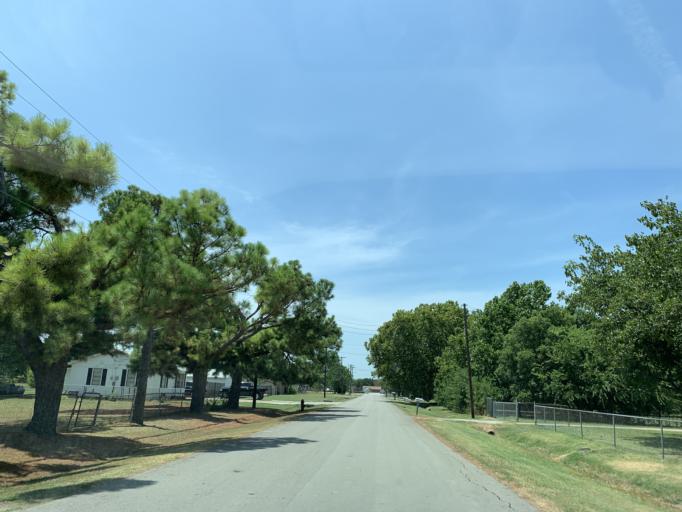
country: US
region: Texas
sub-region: Dallas County
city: Cedar Hill
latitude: 32.6475
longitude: -97.0254
